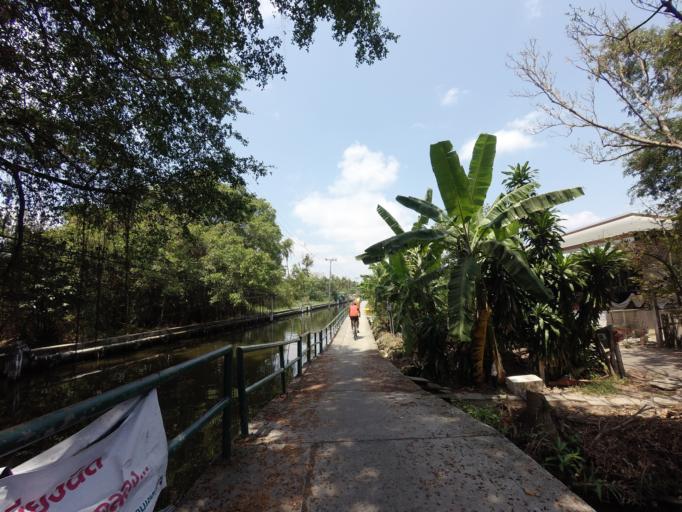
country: TH
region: Bangkok
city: Chom Thong
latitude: 13.6441
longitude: 100.4730
